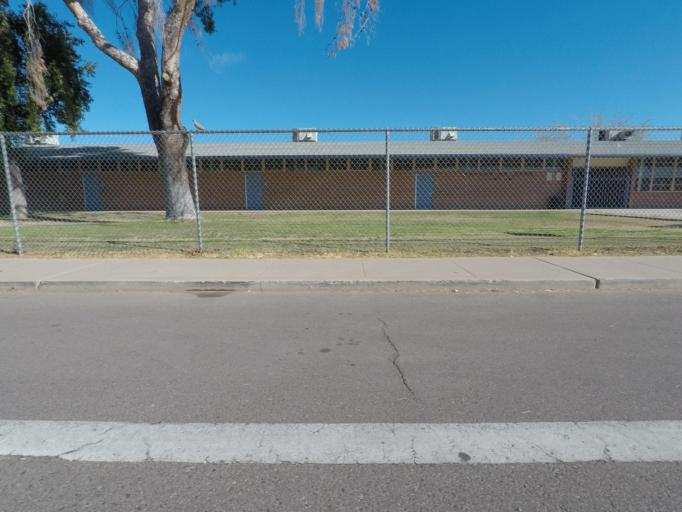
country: US
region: Arizona
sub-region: Maricopa County
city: Glendale
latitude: 33.5314
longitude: -112.1033
